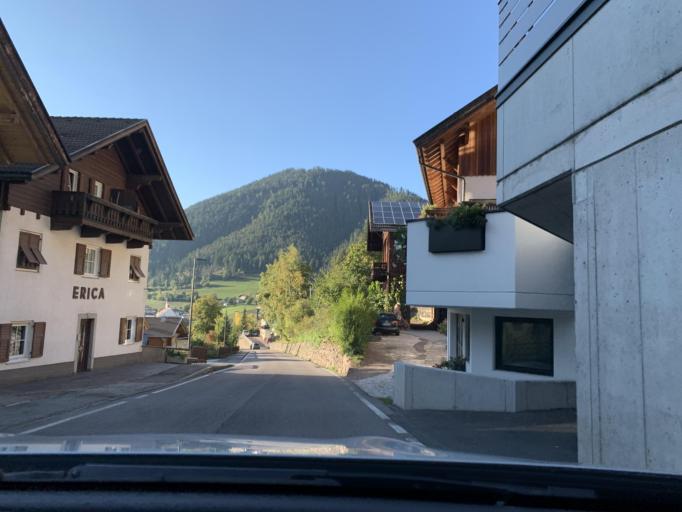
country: IT
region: Trentino-Alto Adige
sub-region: Bolzano
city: Nova Levante
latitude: 46.4268
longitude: 11.5480
